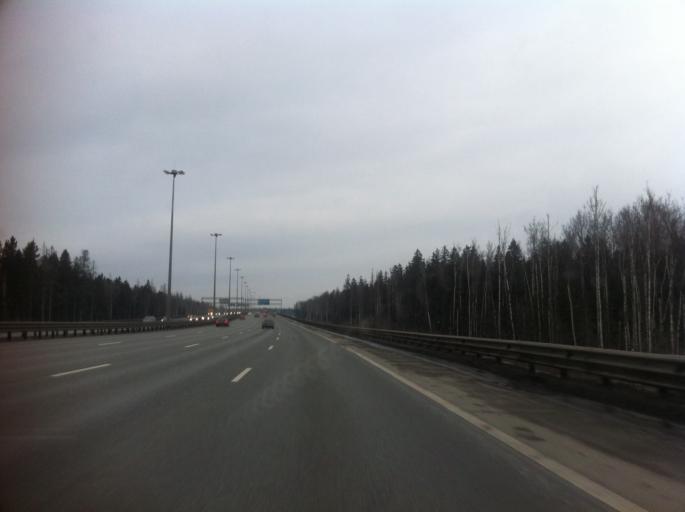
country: RU
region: St.-Petersburg
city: Krasnogvargeisky
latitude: 59.9139
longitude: 30.5260
